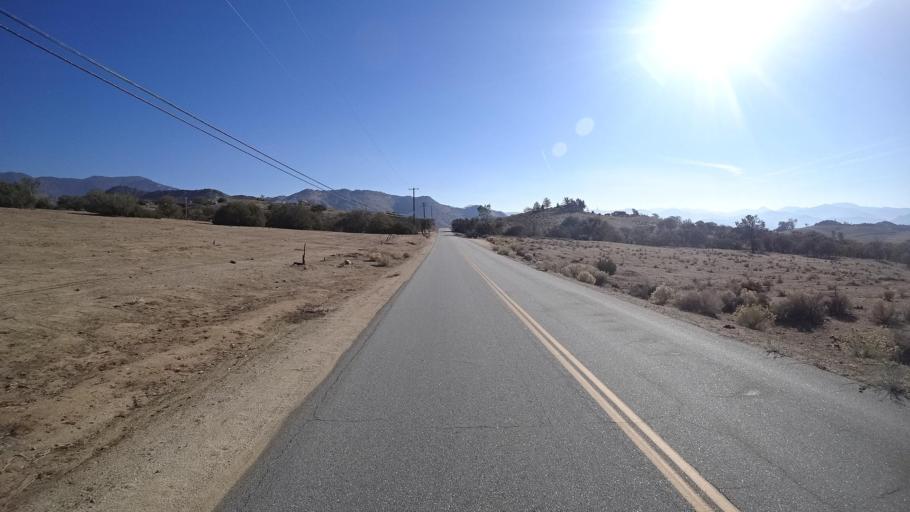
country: US
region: California
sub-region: Kern County
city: Bodfish
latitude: 35.3691
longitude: -118.3933
